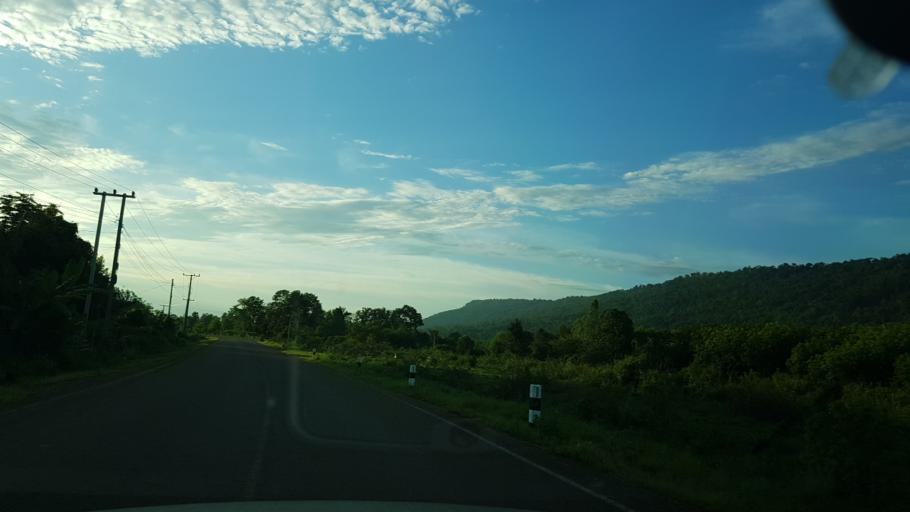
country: TH
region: Nong Khai
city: Sangkhom
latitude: 18.1428
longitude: 102.2791
